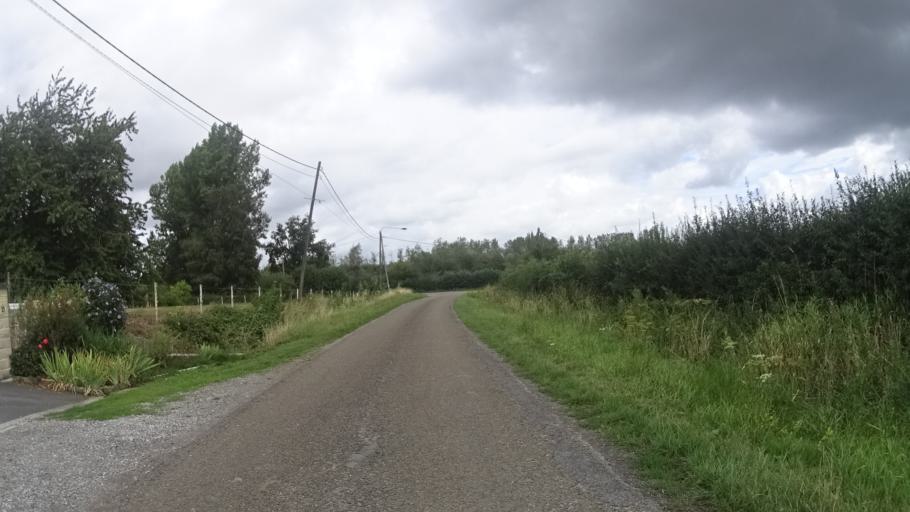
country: FR
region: Nord-Pas-de-Calais
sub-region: Departement du Nord
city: Landrecies
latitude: 50.1270
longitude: 3.7181
